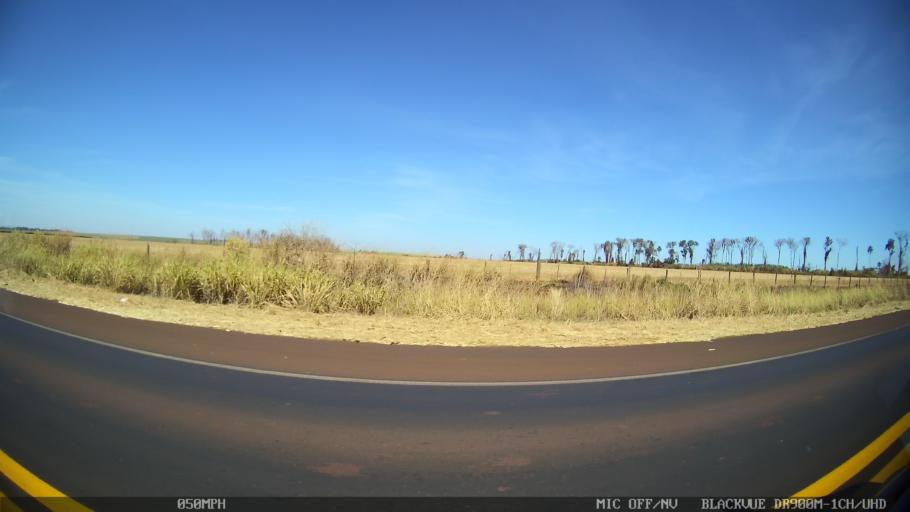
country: BR
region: Sao Paulo
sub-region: Barretos
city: Barretos
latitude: -20.4867
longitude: -48.5147
